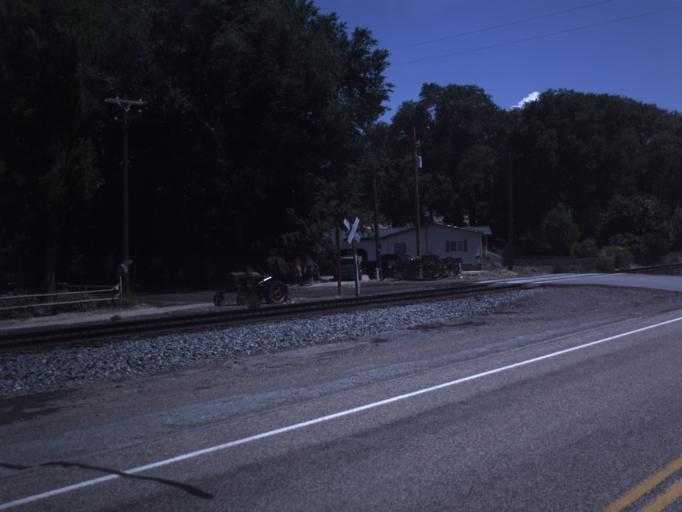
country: US
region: Utah
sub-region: Millard County
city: Delta
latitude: 39.5356
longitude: -112.2774
